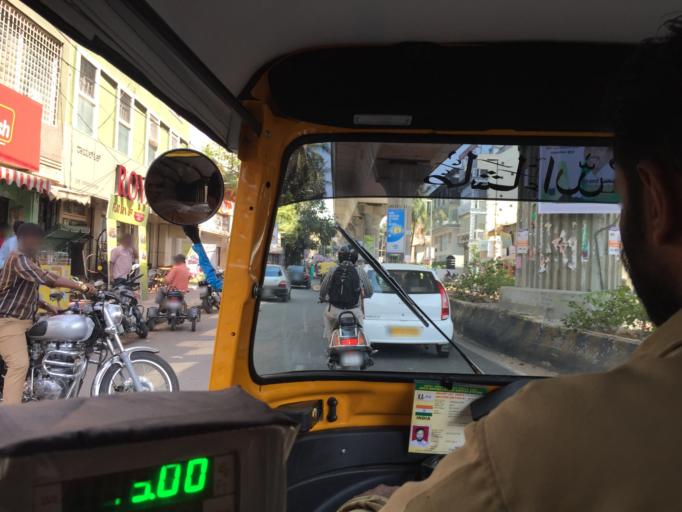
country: IN
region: Karnataka
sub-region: Bangalore Urban
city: Bangalore
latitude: 12.9782
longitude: 77.6331
